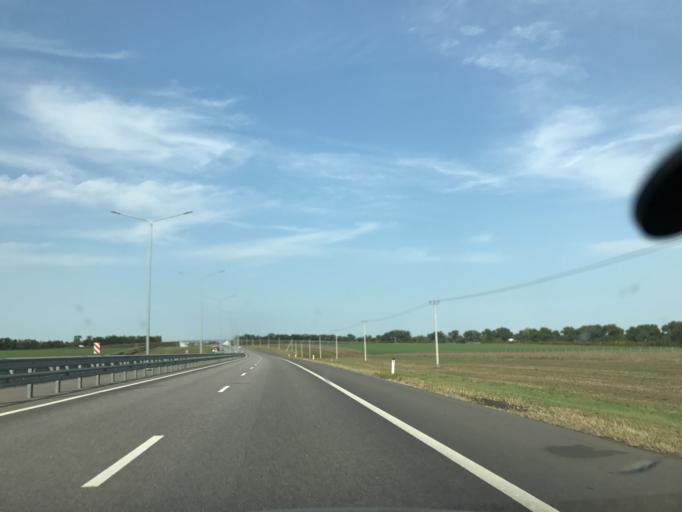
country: RU
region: Voronezj
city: Podkletnoye
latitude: 51.5261
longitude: 39.5105
